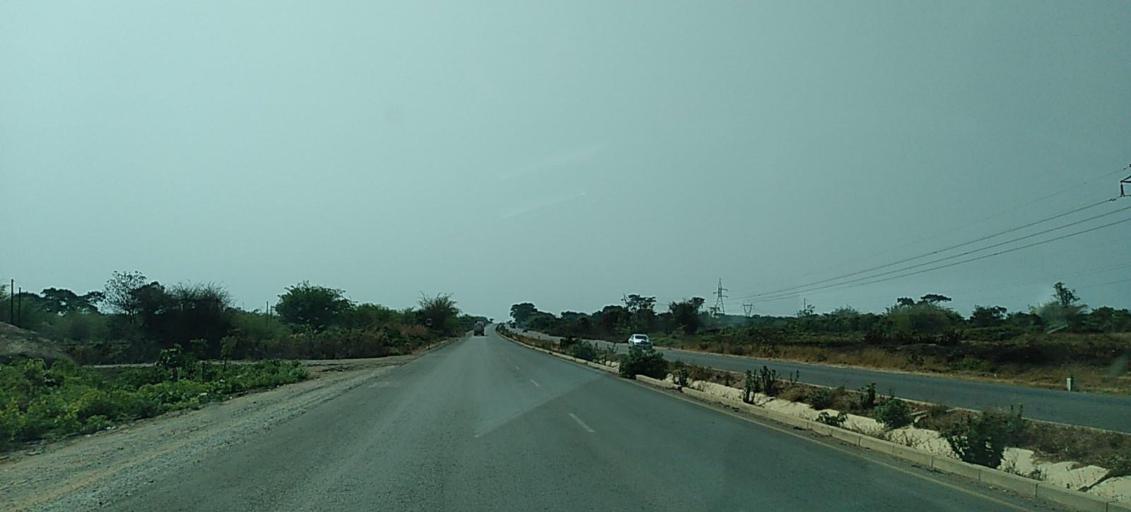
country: ZM
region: Copperbelt
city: Chingola
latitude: -12.5765
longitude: 27.9194
